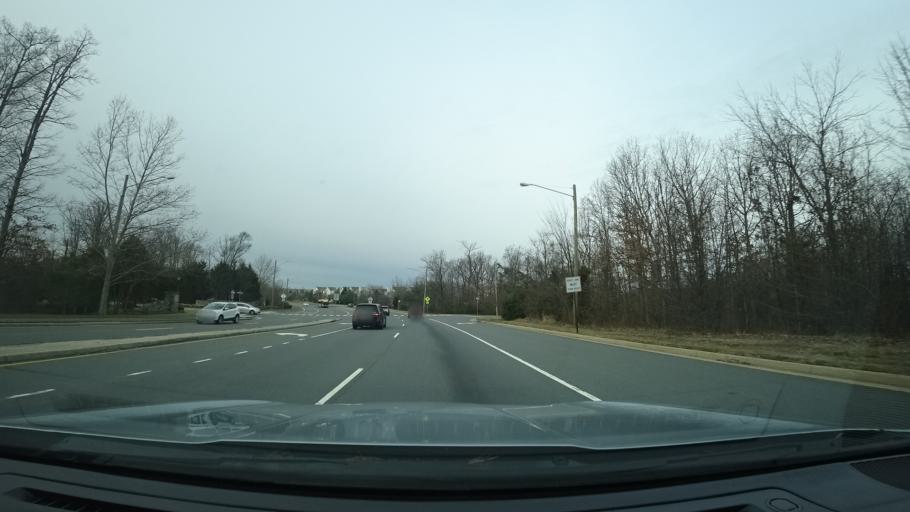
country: US
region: Virginia
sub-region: Fairfax County
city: Floris
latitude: 38.9459
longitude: -77.3947
